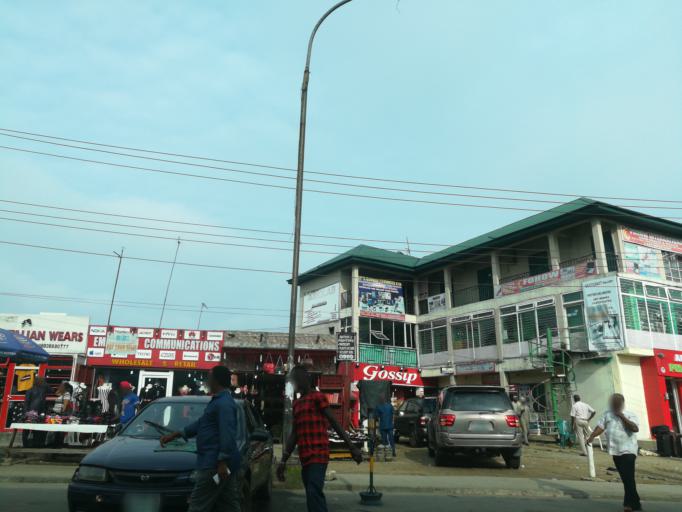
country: NG
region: Rivers
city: Port Harcourt
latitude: 4.8321
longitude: 7.0048
